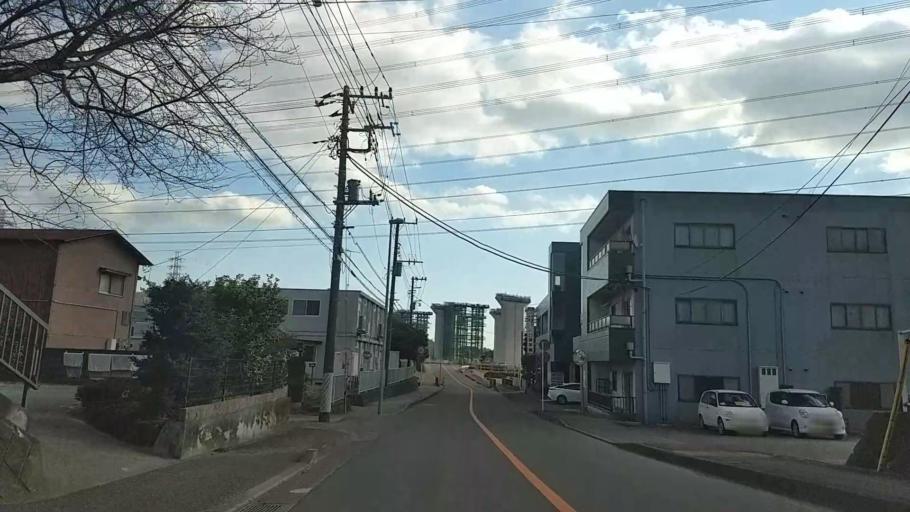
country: JP
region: Kanagawa
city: Isehara
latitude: 35.4172
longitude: 139.2997
